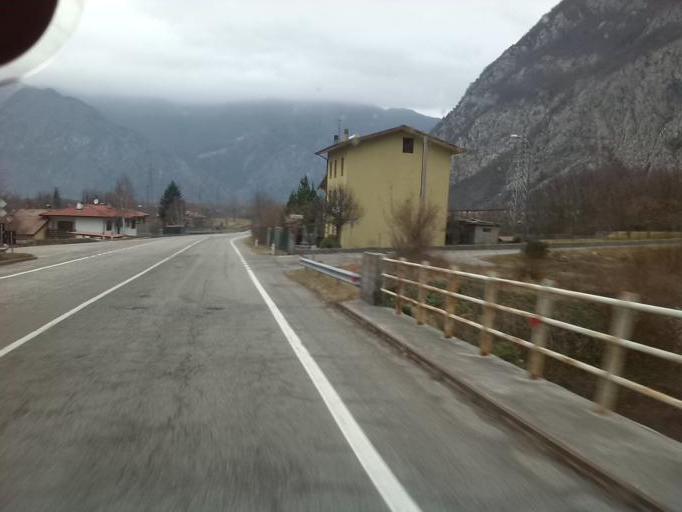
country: IT
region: Friuli Venezia Giulia
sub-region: Provincia di Udine
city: Venzone
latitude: 46.3539
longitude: 13.1396
